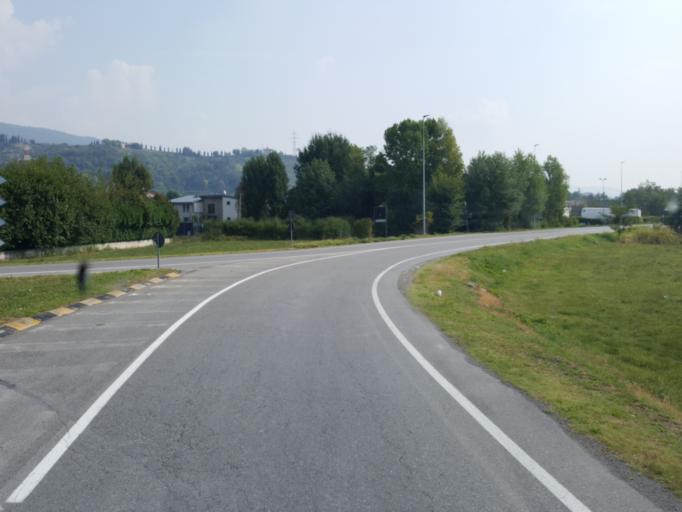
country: IT
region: Lombardy
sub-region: Provincia di Bergamo
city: Telgate
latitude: 45.6371
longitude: 9.8529
